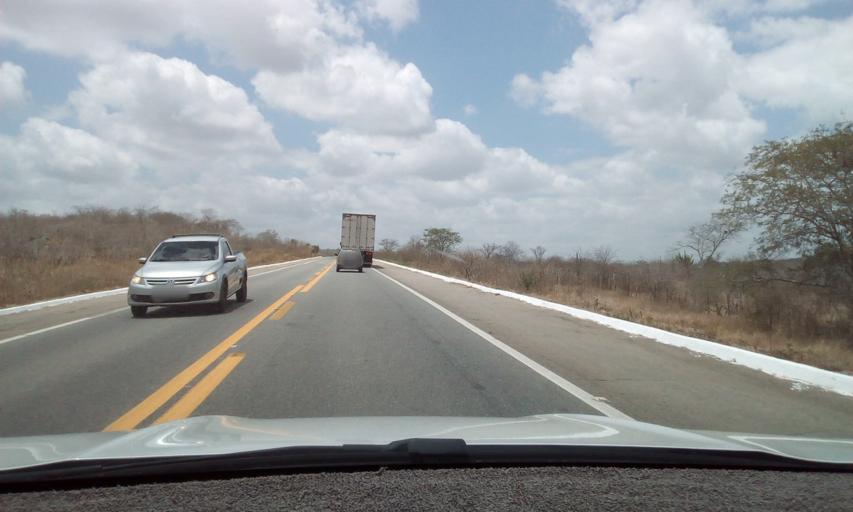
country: BR
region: Pernambuco
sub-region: Taquaritinga Do Norte
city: Taquaritinga do Norte
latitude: -7.7194
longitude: -36.0730
